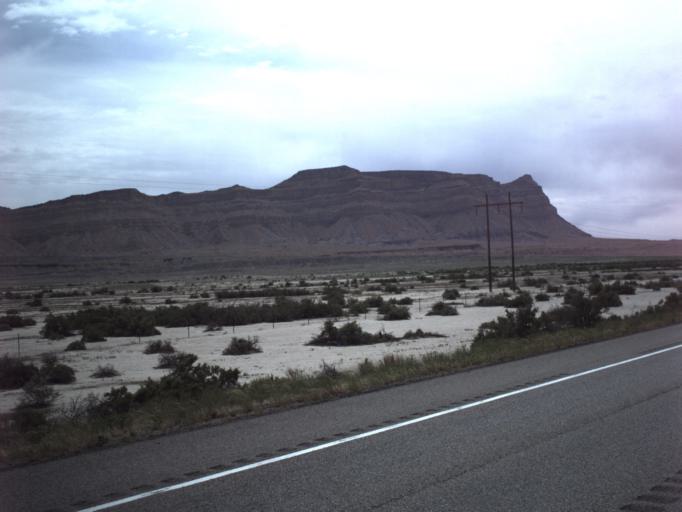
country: US
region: Utah
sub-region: Carbon County
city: East Carbon City
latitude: 39.2450
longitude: -110.3389
